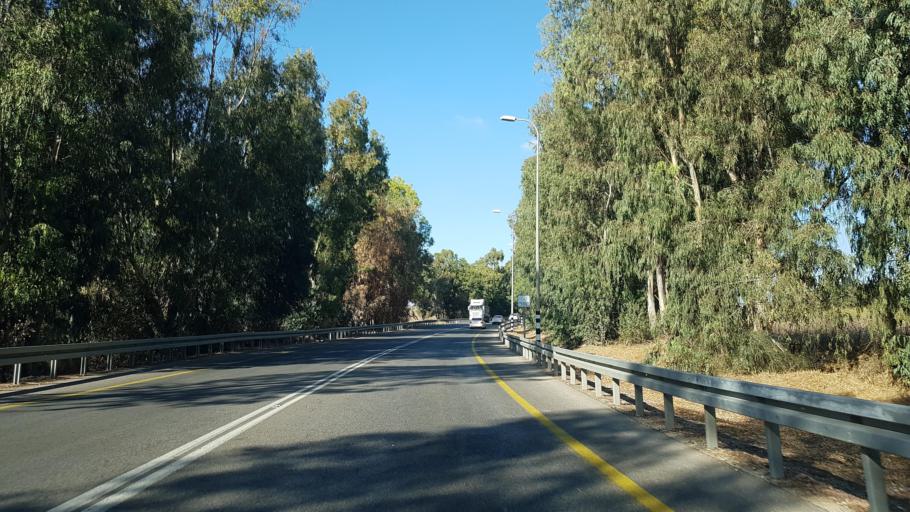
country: PS
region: West Bank
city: Tulkarm
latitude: 32.3540
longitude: 35.0146
